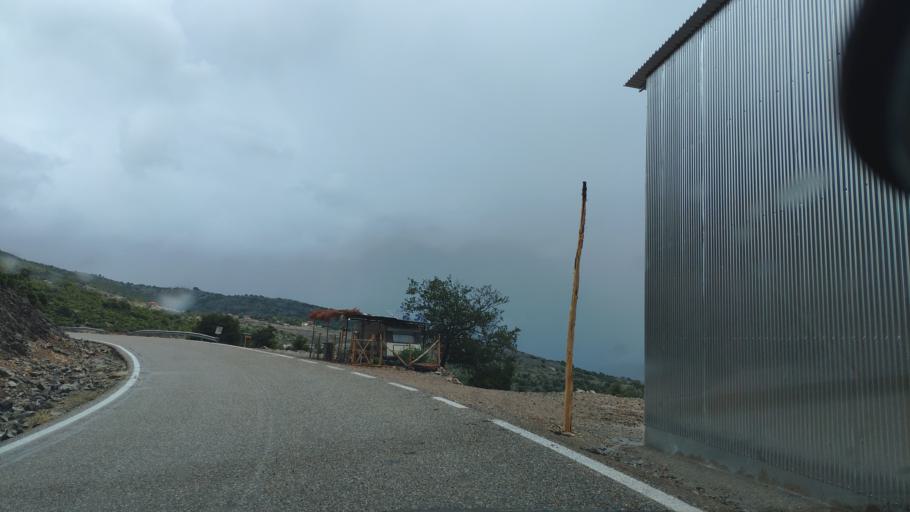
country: GR
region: West Greece
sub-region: Nomos Aitolias kai Akarnanias
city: Krikellos
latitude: 39.0691
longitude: 21.3837
